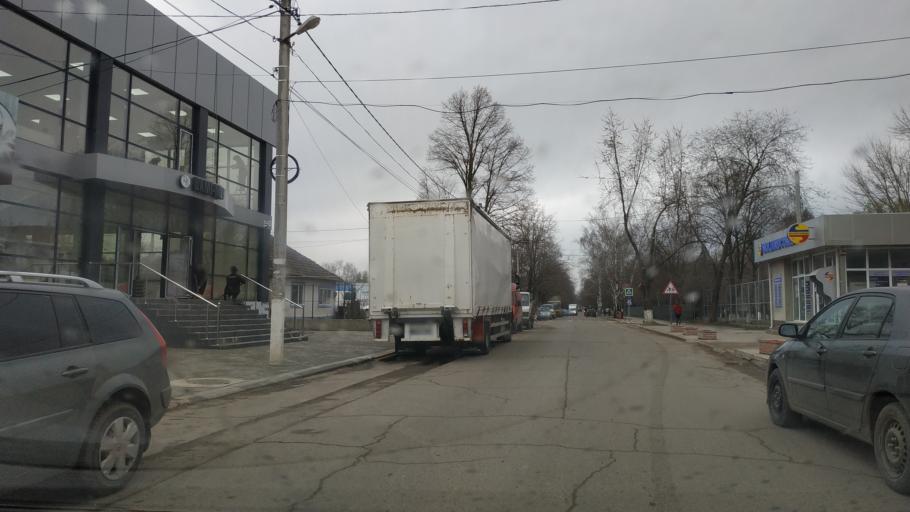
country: MD
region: Leova
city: Leova
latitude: 46.4832
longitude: 28.2512
